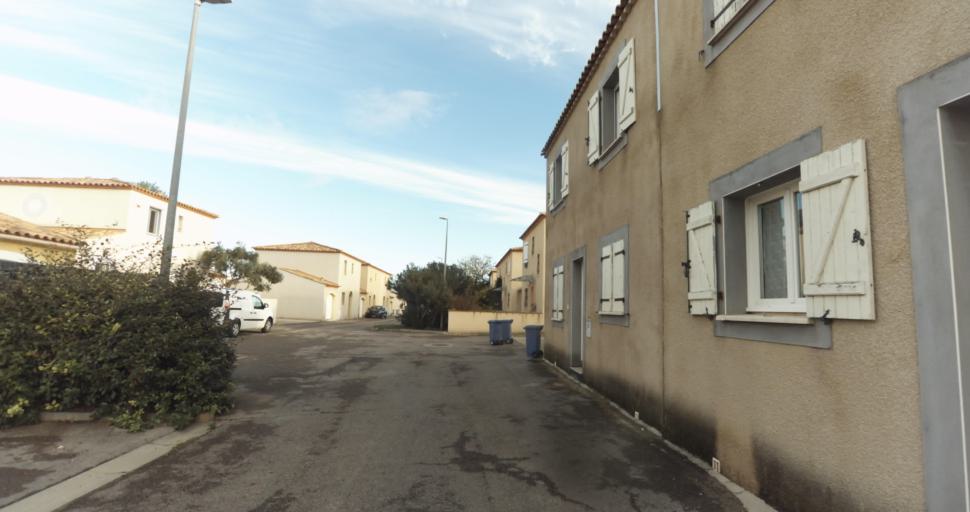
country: FR
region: Languedoc-Roussillon
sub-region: Departement du Gard
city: Aigues-Mortes
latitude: 43.5641
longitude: 4.2078
